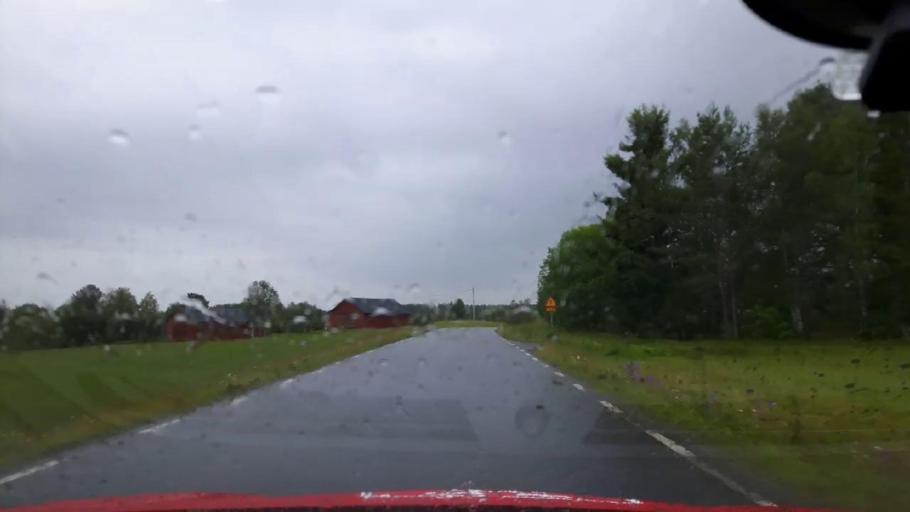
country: SE
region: Jaemtland
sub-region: OEstersunds Kommun
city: Brunflo
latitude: 63.0128
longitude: 14.7331
